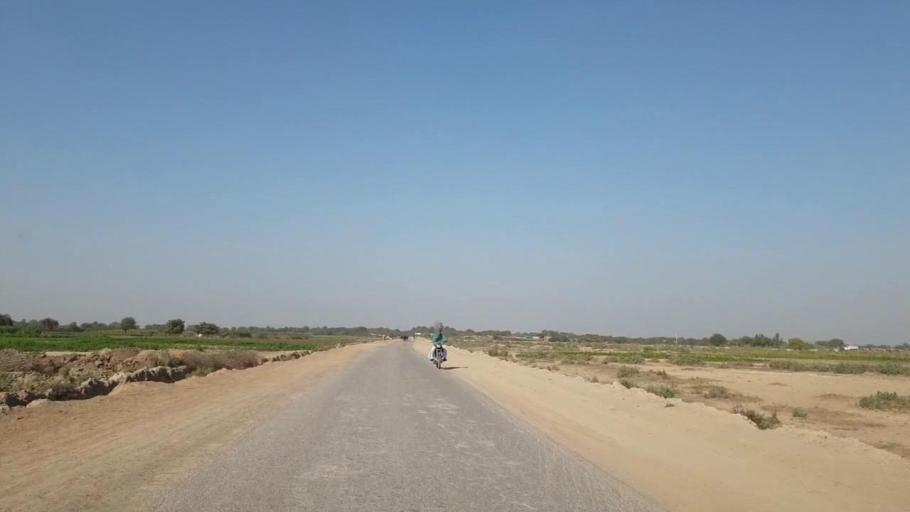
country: PK
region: Sindh
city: Digri
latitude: 25.1154
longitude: 69.1081
